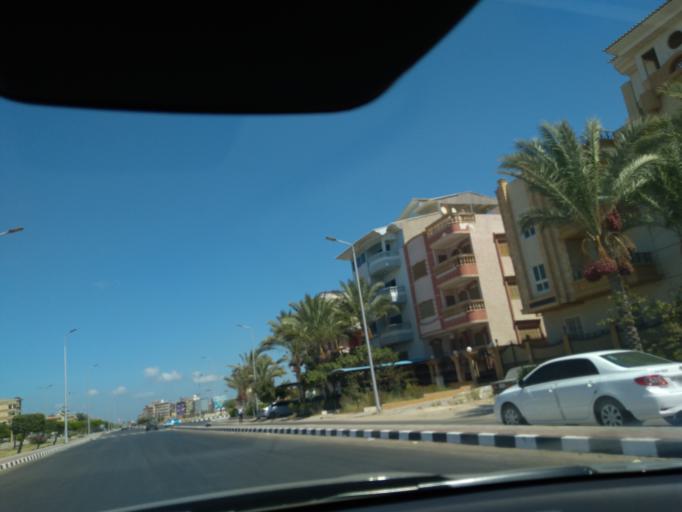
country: EG
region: Dumyat
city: Faraskur
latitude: 31.4345
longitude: 31.6718
